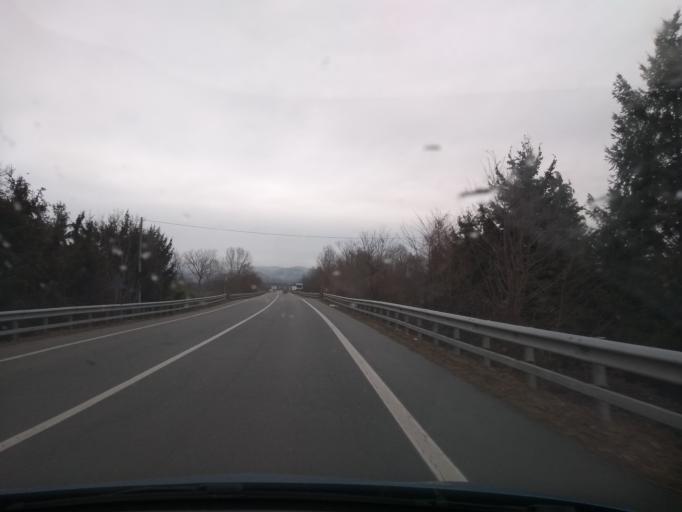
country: IT
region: Piedmont
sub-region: Provincia di Torino
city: Castellamonte
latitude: 45.3725
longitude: 7.7305
